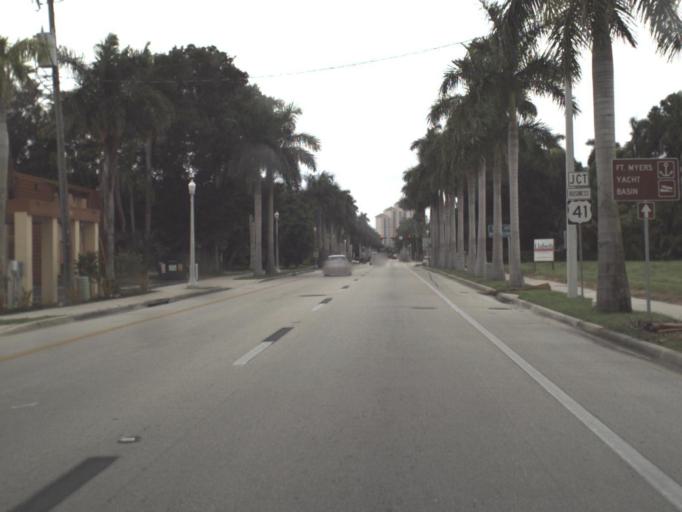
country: US
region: Florida
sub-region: Lee County
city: North Fort Myers
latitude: 26.6495
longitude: -81.8608
